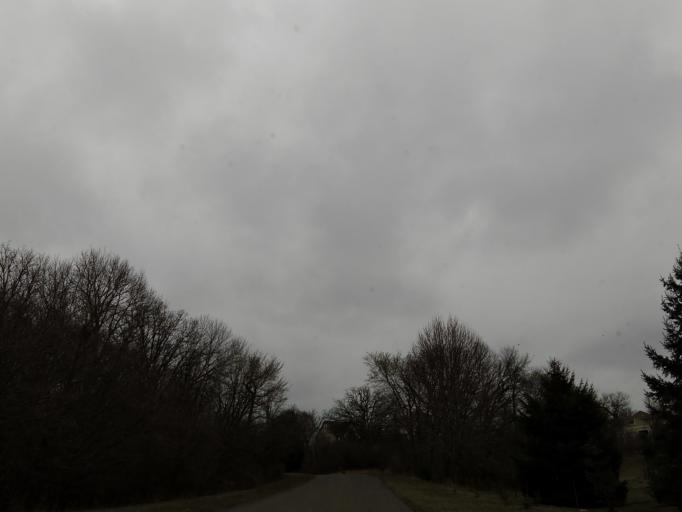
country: US
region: Minnesota
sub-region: Washington County
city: Lakeland
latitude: 44.9718
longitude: -92.7963
